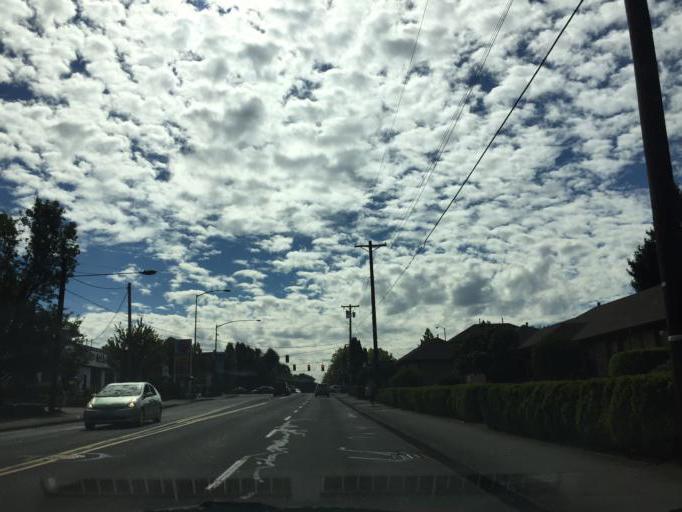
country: US
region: Oregon
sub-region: Clackamas County
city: Milwaukie
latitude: 45.4986
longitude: -122.6227
